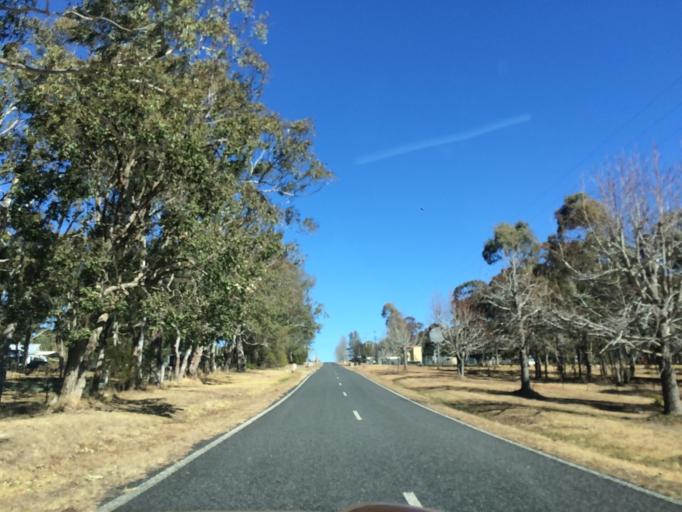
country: AU
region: Queensland
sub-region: Southern Downs
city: Stanthorpe
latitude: -28.6430
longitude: 152.0855
